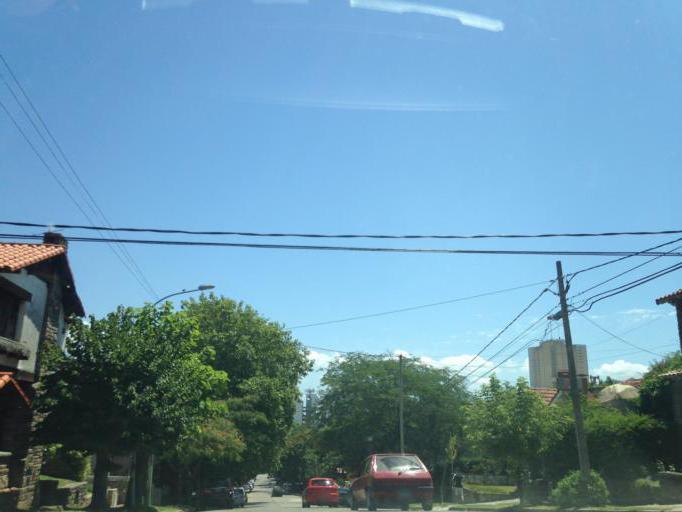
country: AR
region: Buenos Aires
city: Mar del Plata
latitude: -38.0141
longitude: -57.5360
